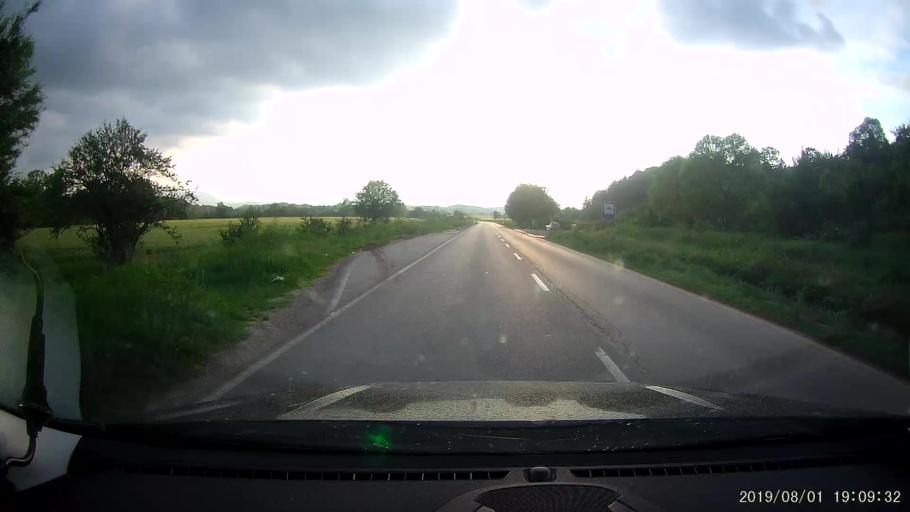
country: BG
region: Shumen
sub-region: Obshtina Smyadovo
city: Smyadovo
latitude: 42.9846
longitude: 27.0012
